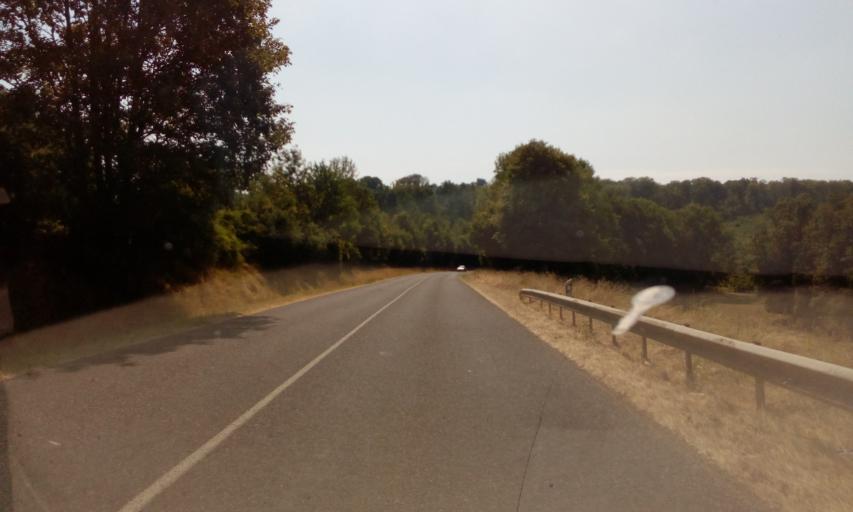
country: FR
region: Lorraine
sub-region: Departement de la Meuse
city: Montmedy
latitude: 49.4973
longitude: 5.3911
